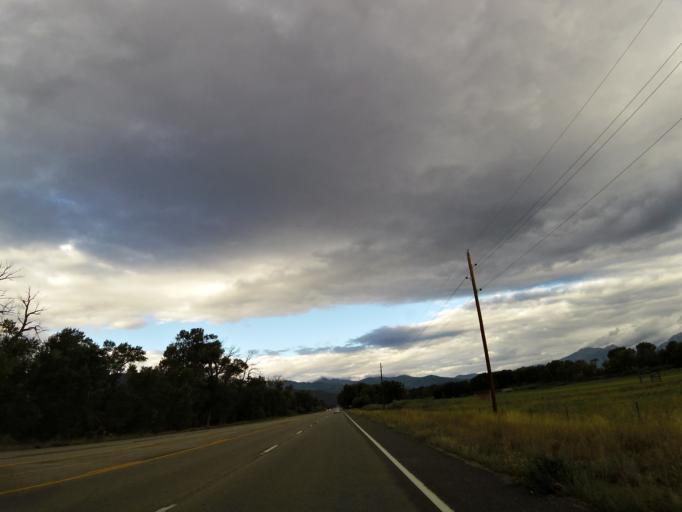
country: US
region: Colorado
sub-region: Chaffee County
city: Salida
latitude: 38.5209
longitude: -106.0359
